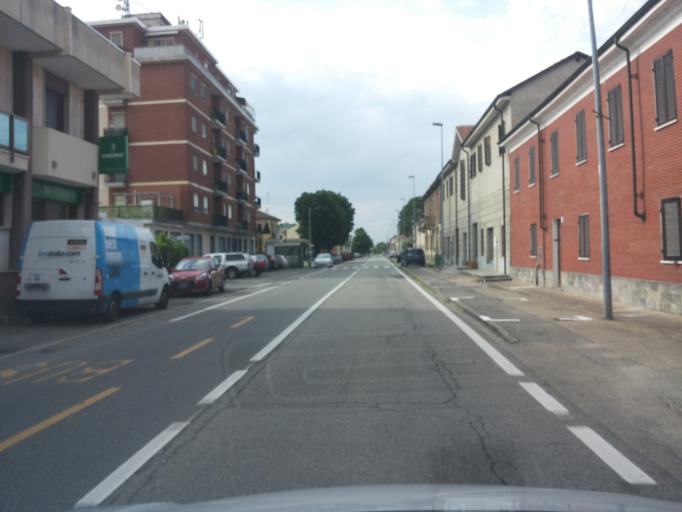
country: IT
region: Piedmont
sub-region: Provincia di Vercelli
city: Vercelli
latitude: 45.3060
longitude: 8.4443
